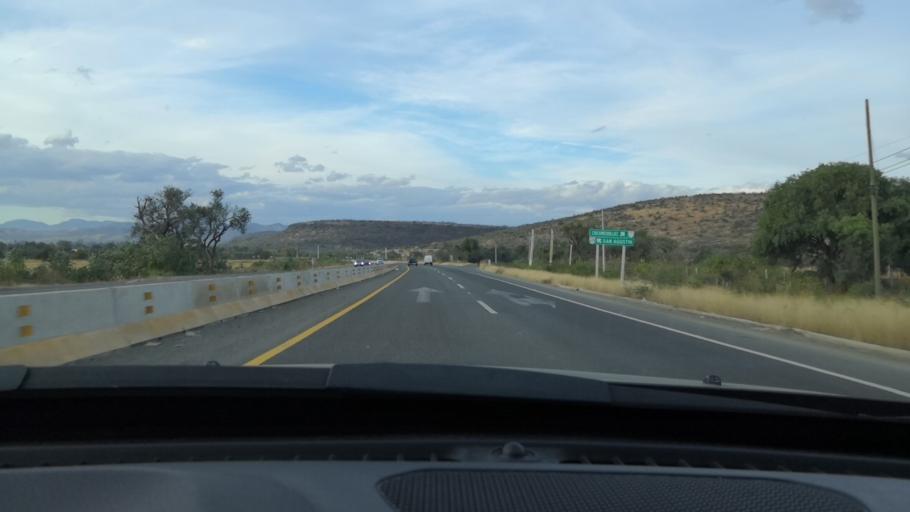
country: MX
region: Guanajuato
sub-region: Silao de la Victoria
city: Colonia Francisco Javier Mina
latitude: 21.0141
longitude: -101.4351
